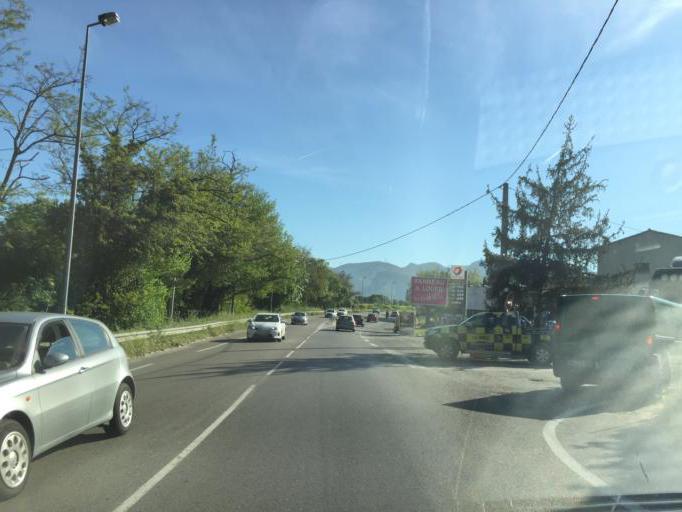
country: FR
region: Provence-Alpes-Cote d'Azur
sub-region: Departement des Bouches-du-Rhone
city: Aubagne
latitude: 43.2967
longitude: 5.5847
